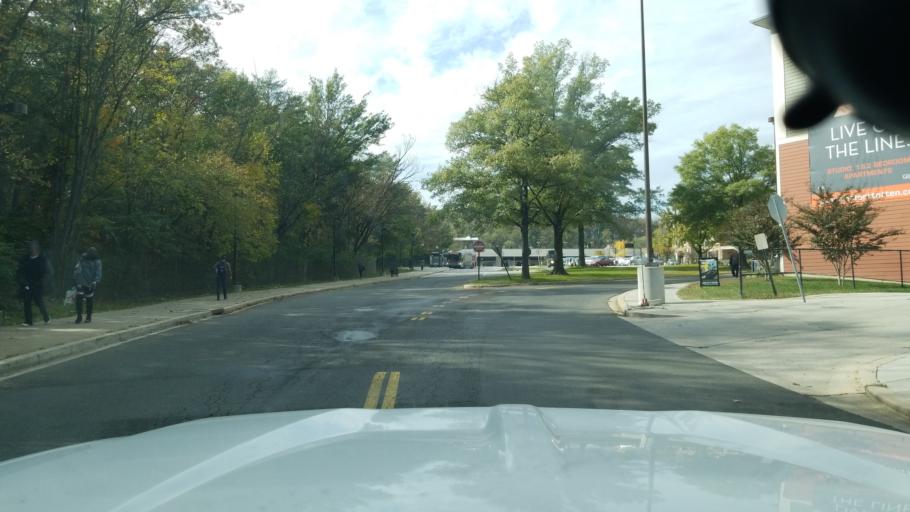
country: US
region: Maryland
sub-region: Prince George's County
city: Chillum
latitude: 38.9525
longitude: -76.9993
